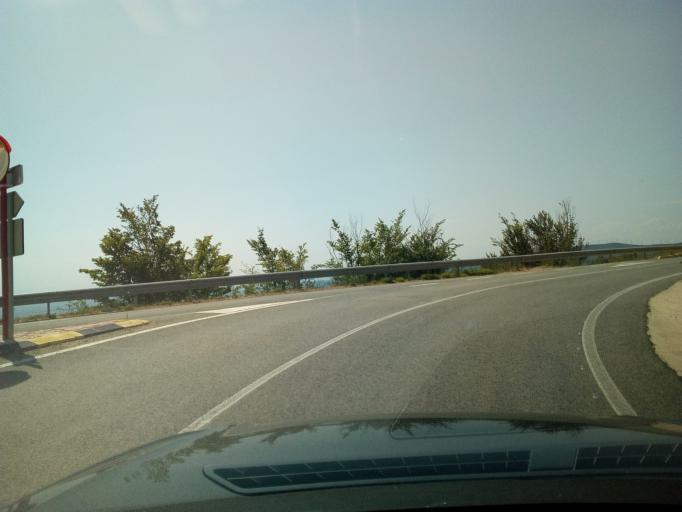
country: ES
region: Navarre
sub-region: Provincia de Navarra
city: Ujue
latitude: 42.5141
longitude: -1.5107
